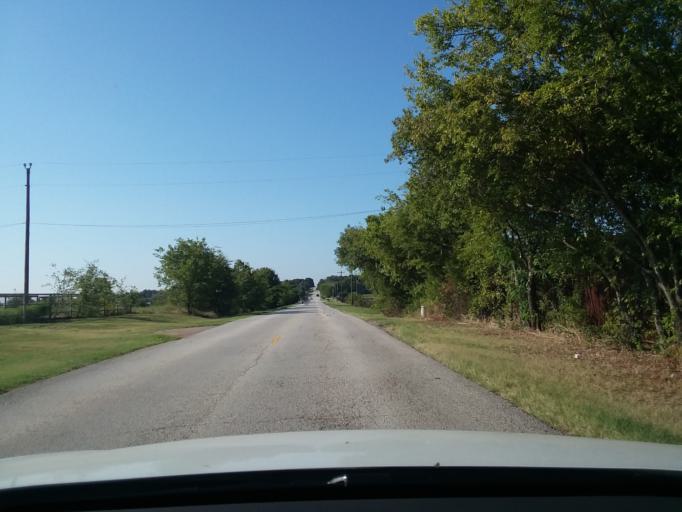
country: US
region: Texas
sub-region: Denton County
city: Bartonville
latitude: 33.0708
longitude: -97.1316
